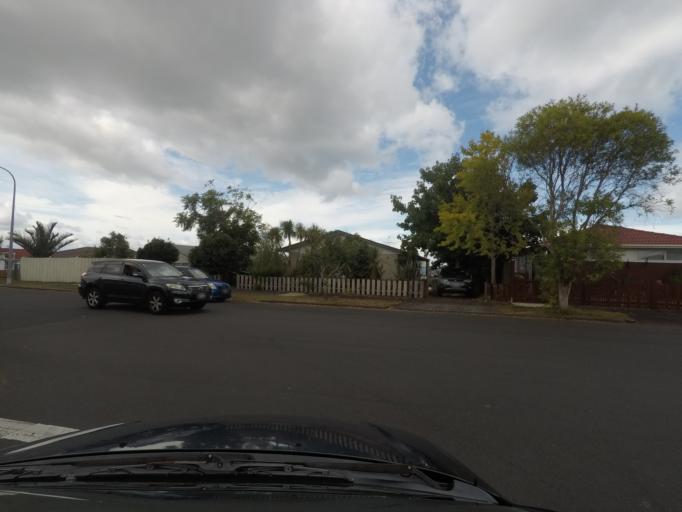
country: NZ
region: Auckland
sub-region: Auckland
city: Rosebank
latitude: -36.9090
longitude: 174.7108
